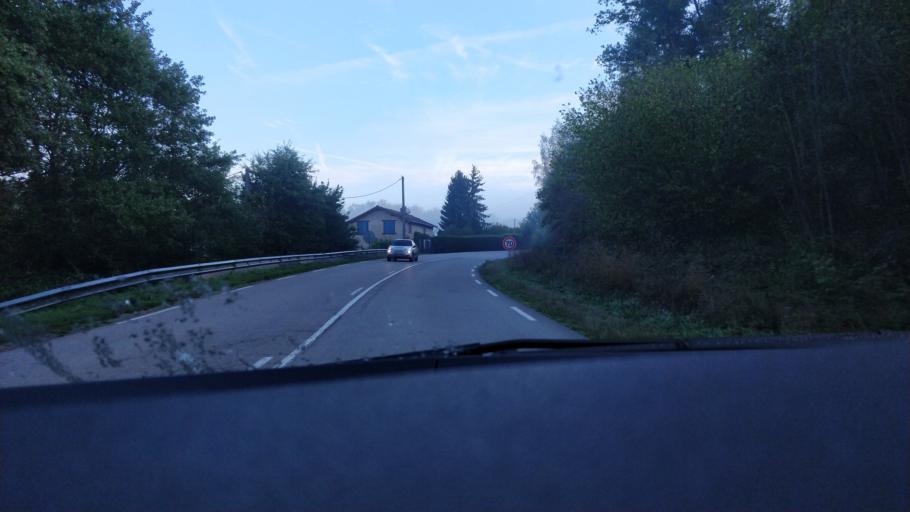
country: FR
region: Limousin
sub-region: Departement de la Haute-Vienne
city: Saint-Leonard-de-Noblat
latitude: 45.8487
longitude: 1.4943
